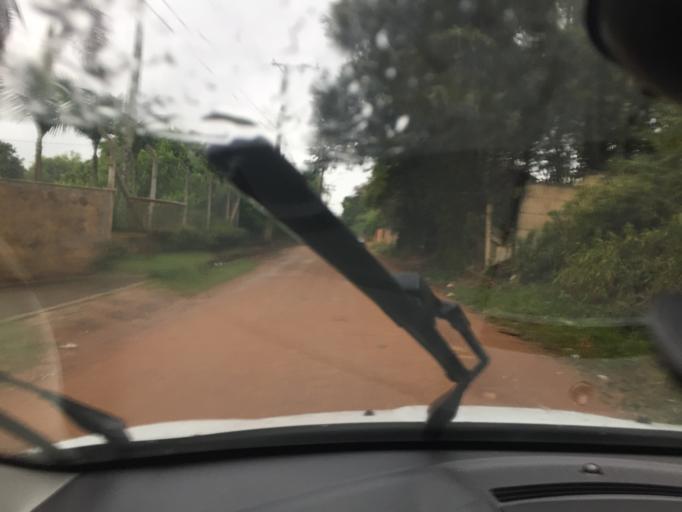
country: BR
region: Sao Paulo
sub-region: Jarinu
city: Jarinu
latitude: -23.1381
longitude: -46.7241
